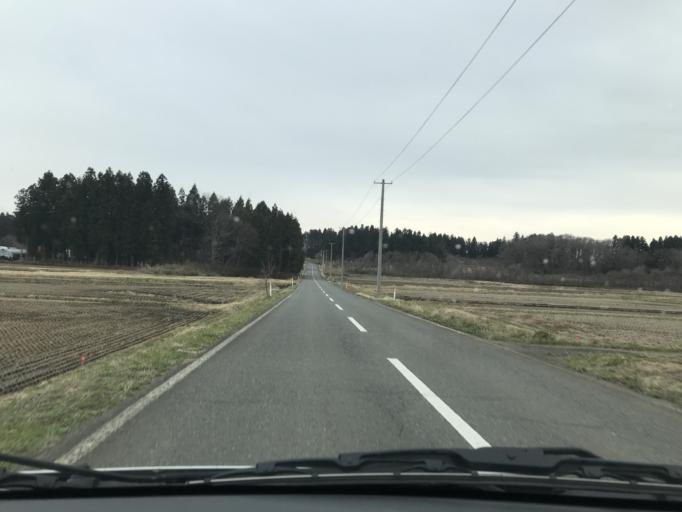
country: JP
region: Iwate
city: Mizusawa
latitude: 39.0957
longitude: 141.0690
